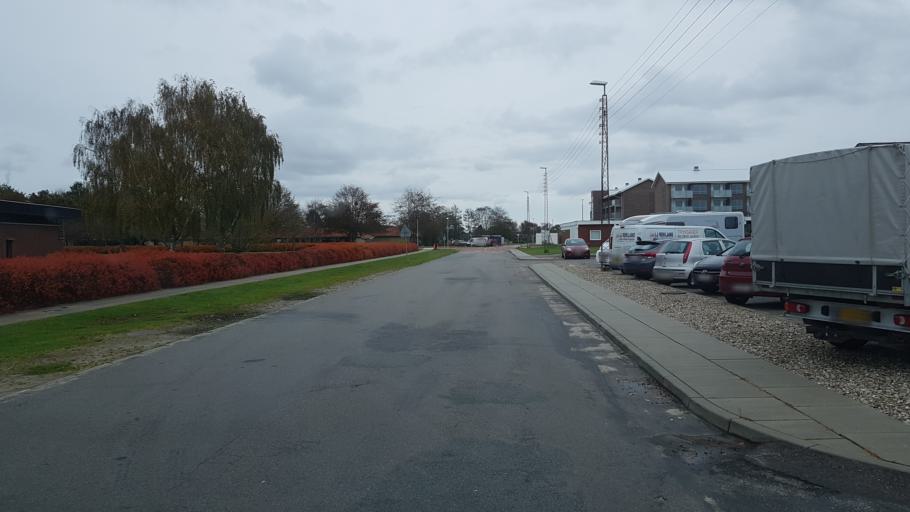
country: DK
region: South Denmark
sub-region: Billund Kommune
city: Grindsted
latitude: 55.7615
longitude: 8.9131
